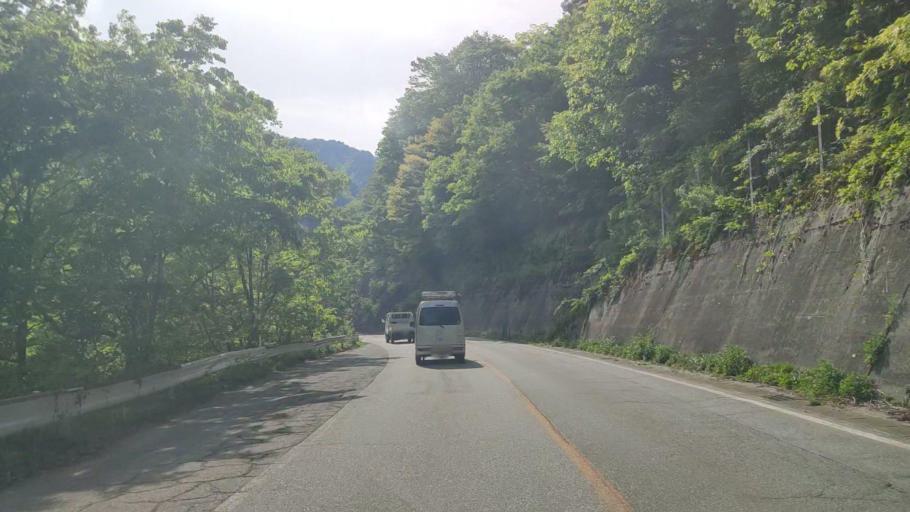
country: JP
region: Gifu
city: Takayama
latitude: 36.2702
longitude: 137.3970
